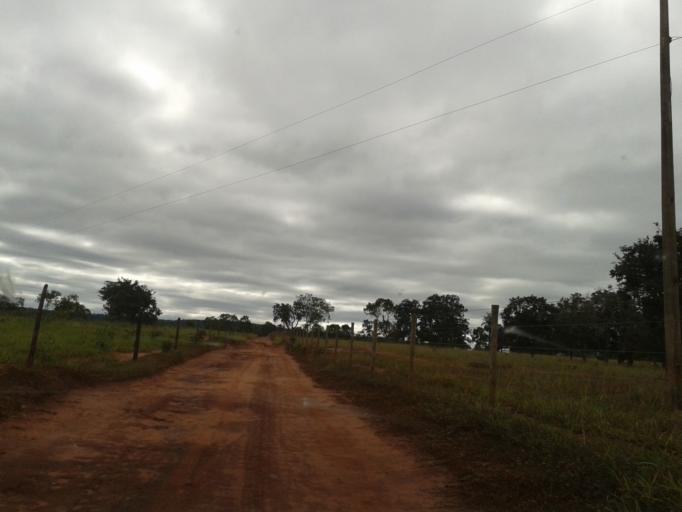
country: BR
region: Minas Gerais
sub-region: Campina Verde
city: Campina Verde
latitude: -19.5064
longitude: -49.6619
